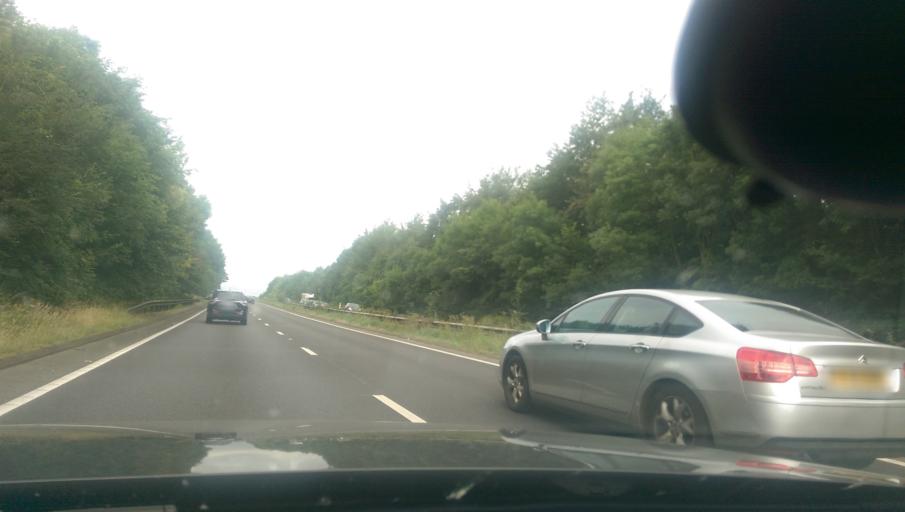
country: GB
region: England
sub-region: Hampshire
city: Andover
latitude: 51.1968
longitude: -1.4933
